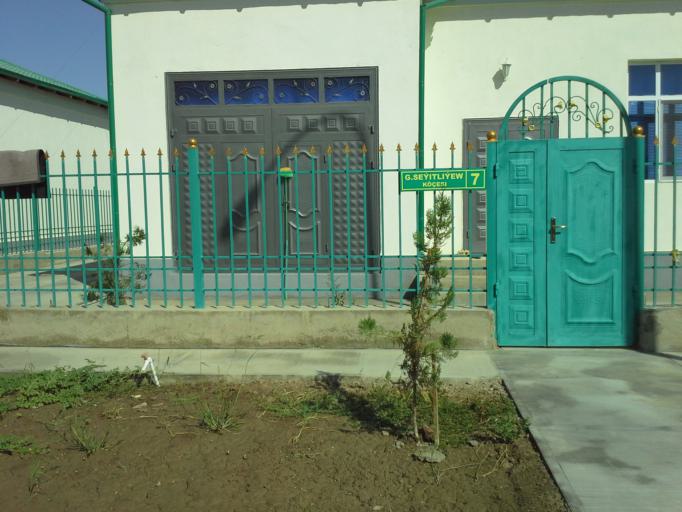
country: TM
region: Dasoguz
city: Dasoguz
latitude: 41.8093
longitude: 59.9476
